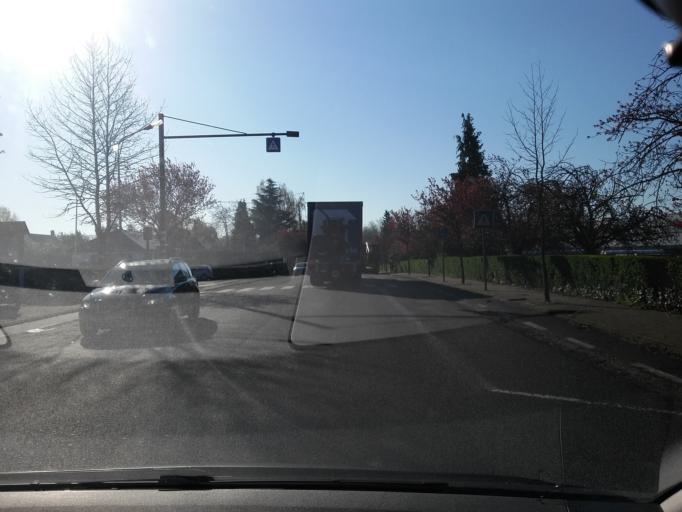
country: BE
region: Wallonia
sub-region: Province du Brabant Wallon
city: Waterloo
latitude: 50.7109
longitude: 4.4025
